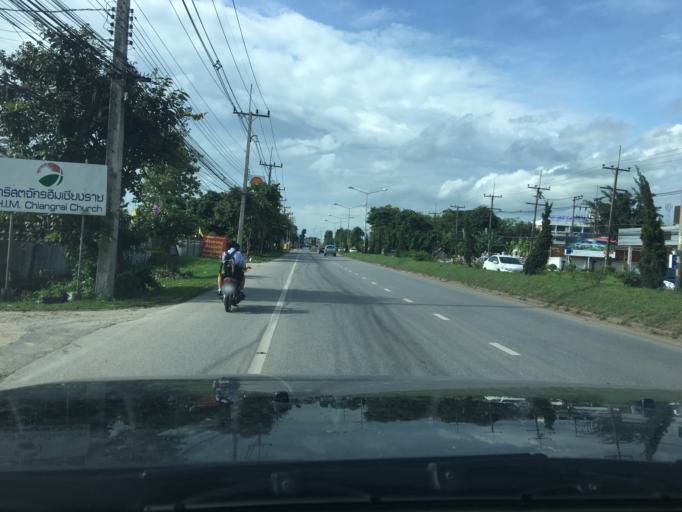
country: TH
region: Chiang Rai
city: Chiang Rai
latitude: 19.9431
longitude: 99.8463
